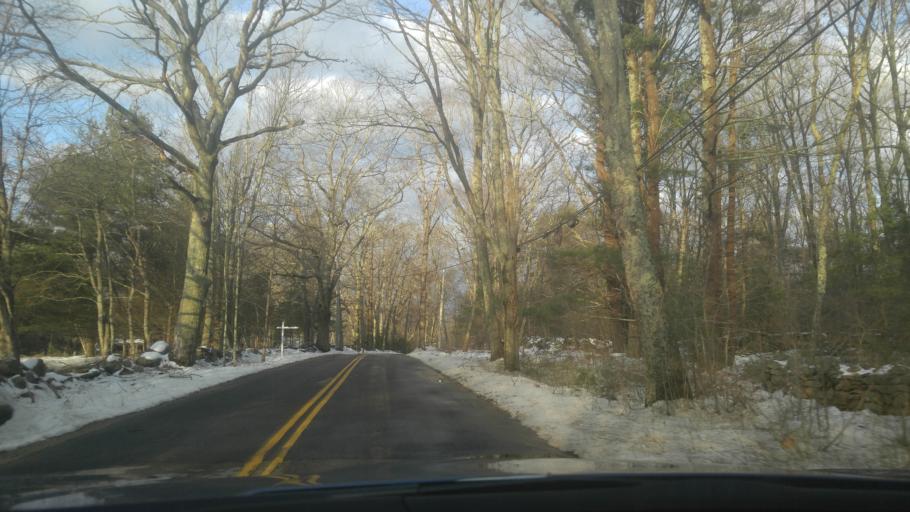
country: US
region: Rhode Island
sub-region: Kent County
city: Coventry
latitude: 41.7172
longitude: -71.6929
